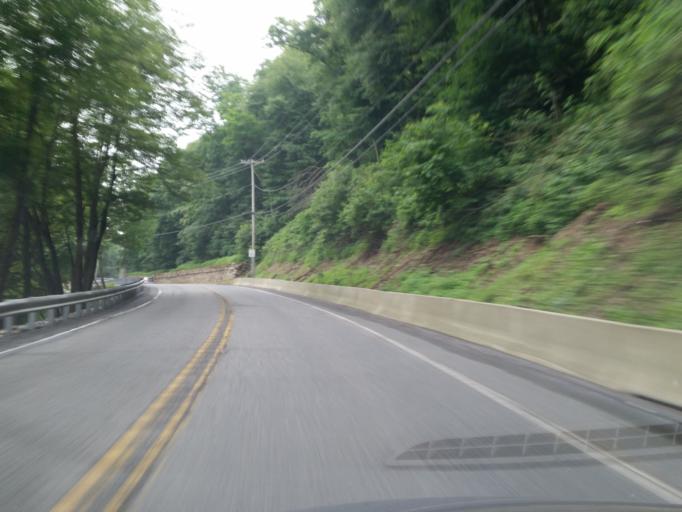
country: US
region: Pennsylvania
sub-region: Lebanon County
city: Jonestown
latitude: 40.4780
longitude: -76.5291
